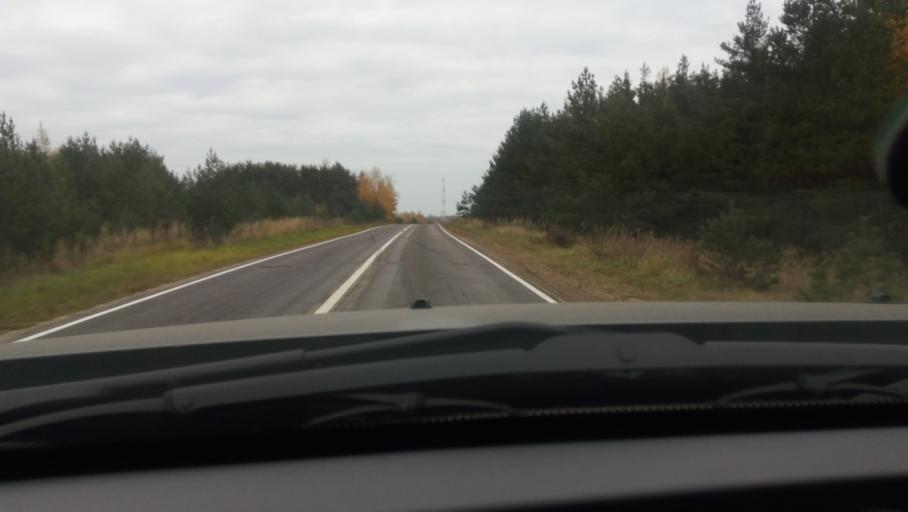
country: RU
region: Moskovskaya
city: Avsyunino
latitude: 55.5979
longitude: 39.2324
